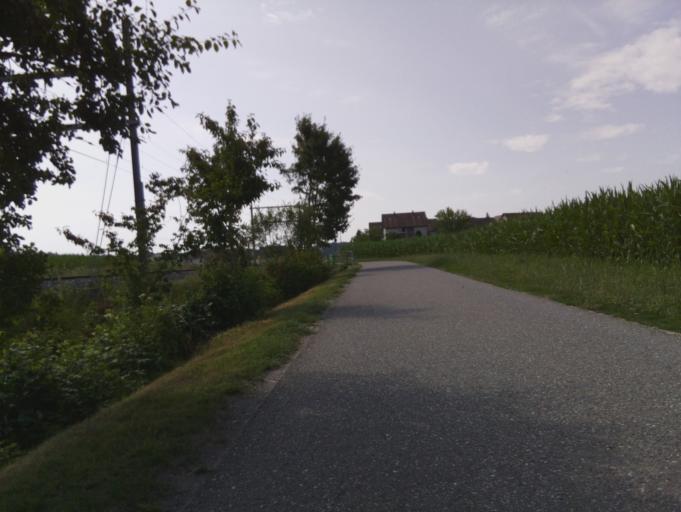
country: CH
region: Zurich
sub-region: Bezirk Andelfingen
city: Henggart
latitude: 47.5691
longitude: 8.6830
